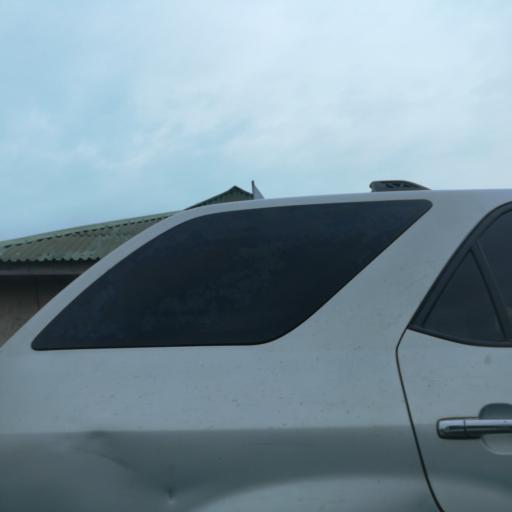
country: NG
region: Lagos
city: Makoko
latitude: 6.4973
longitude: 3.3891
